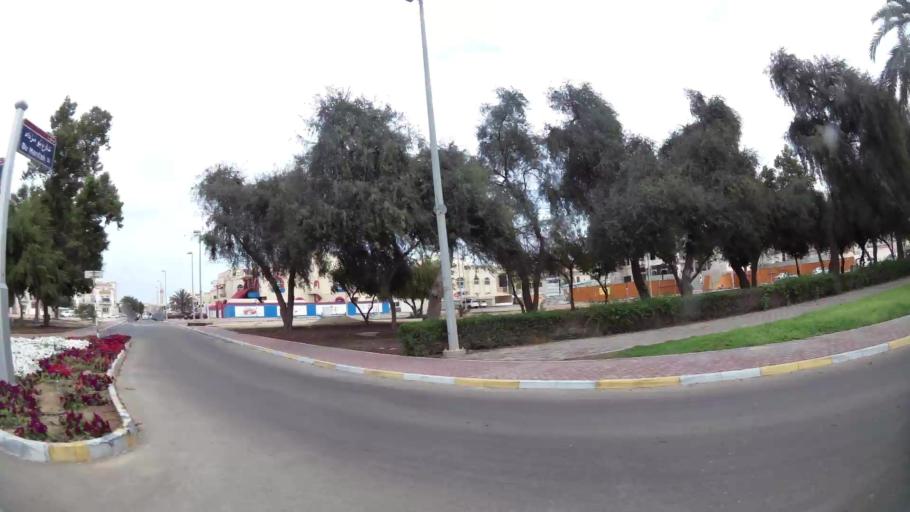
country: AE
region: Abu Dhabi
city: Abu Dhabi
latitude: 24.4316
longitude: 54.4413
